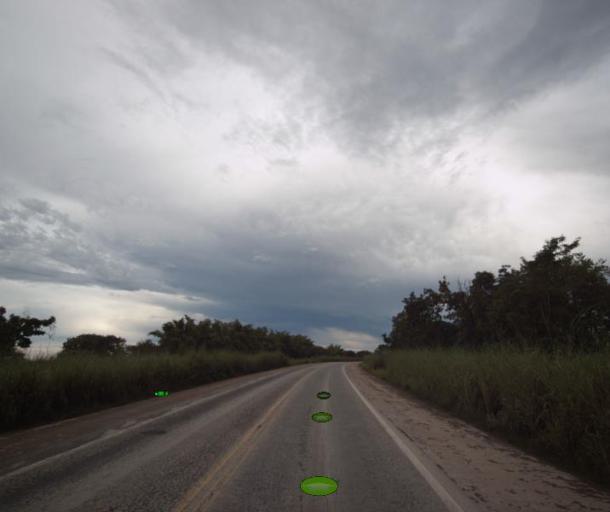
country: BR
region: Goias
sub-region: Porangatu
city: Porangatu
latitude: -13.5571
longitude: -49.0631
